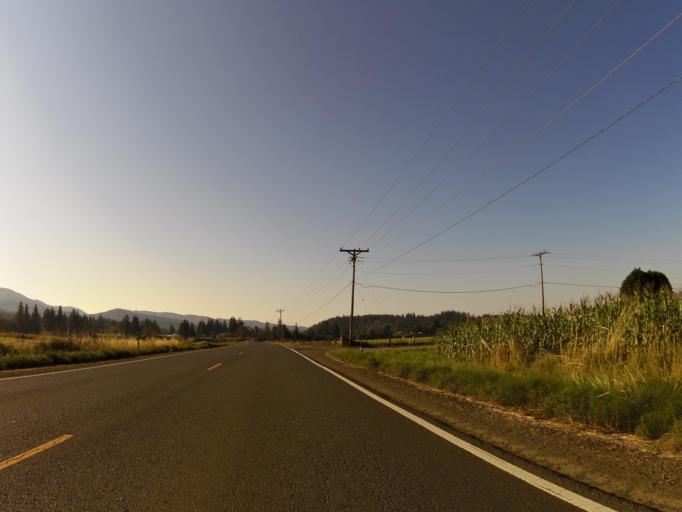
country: US
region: Oregon
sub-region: Tillamook County
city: Tillamook
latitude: 45.4378
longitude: -123.7777
